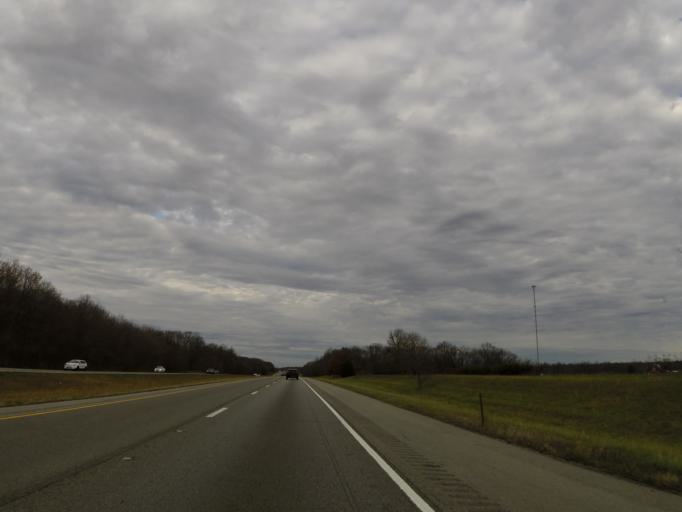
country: US
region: Illinois
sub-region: Clinton County
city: Wamac
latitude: 38.3662
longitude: -89.0879
